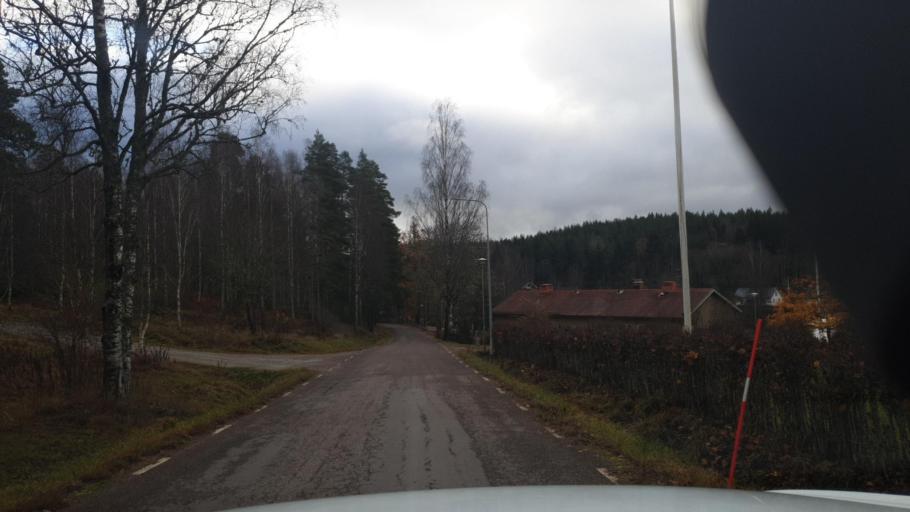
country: SE
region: Vaermland
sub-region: Sunne Kommun
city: Sunne
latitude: 59.6203
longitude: 12.9602
